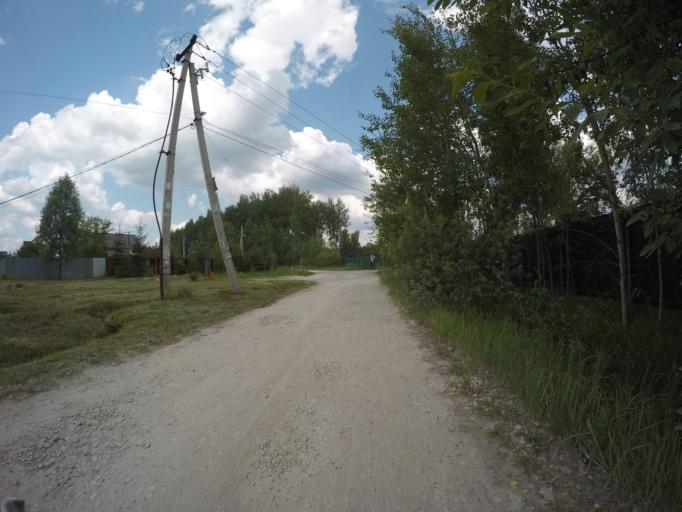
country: RU
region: Moskovskaya
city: Rechitsy
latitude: 55.6064
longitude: 38.5072
